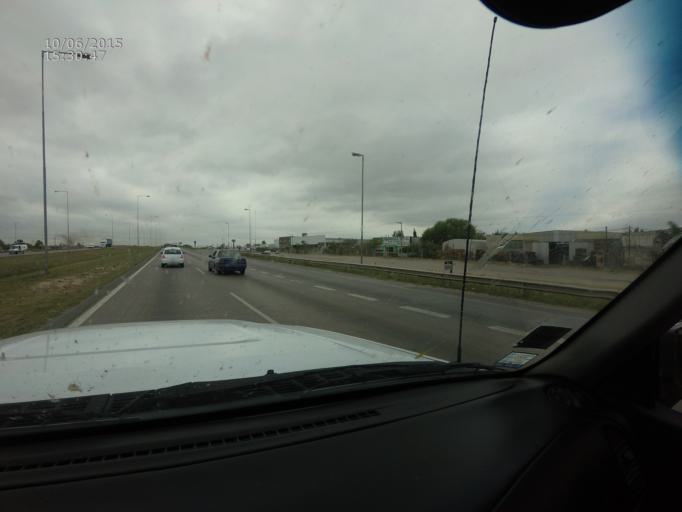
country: AR
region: Cordoba
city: Malvinas Argentinas
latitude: -31.3798
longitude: -64.1269
